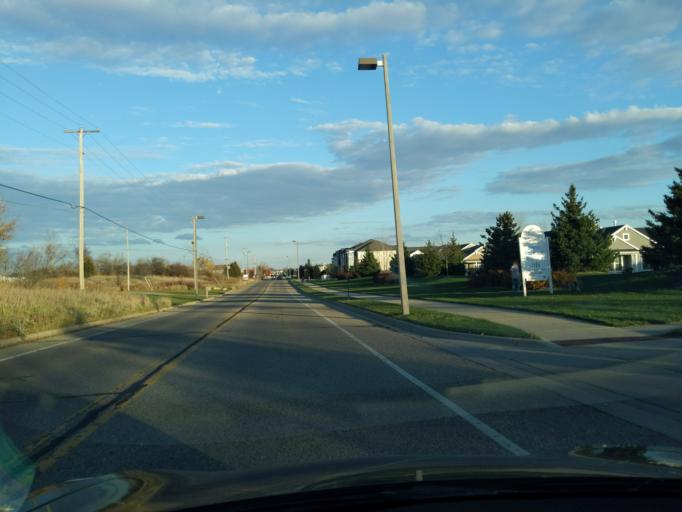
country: US
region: Michigan
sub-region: Ingham County
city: East Lansing
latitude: 42.7731
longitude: -84.5003
